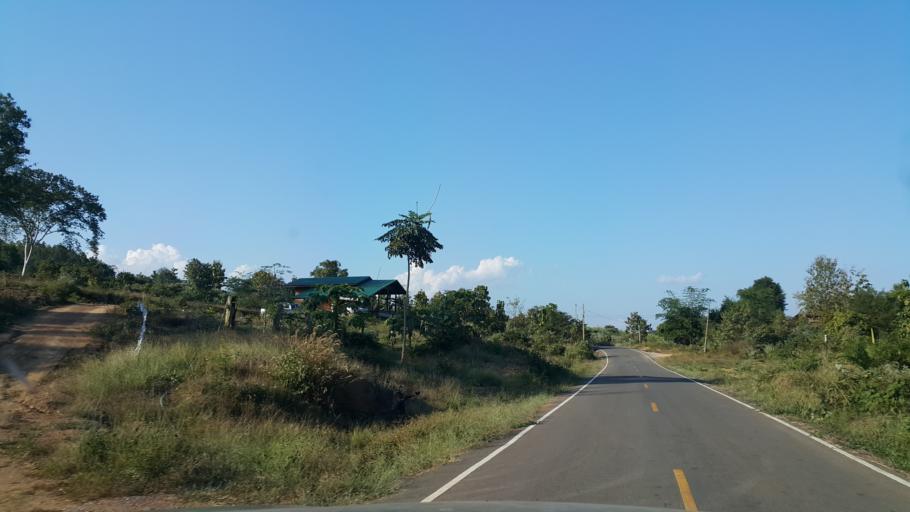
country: TH
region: Sukhothai
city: Thung Saliam
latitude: 17.3940
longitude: 99.5092
